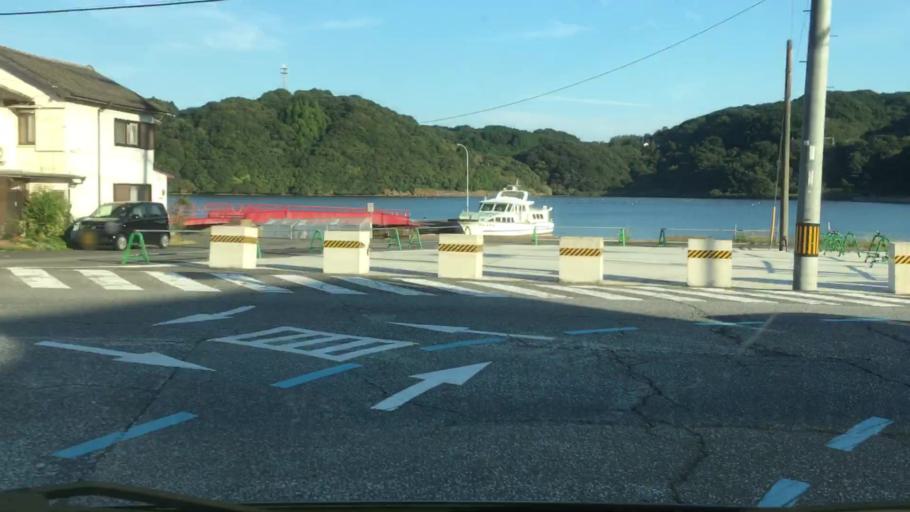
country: JP
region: Nagasaki
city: Sasebo
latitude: 33.0499
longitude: 129.7295
